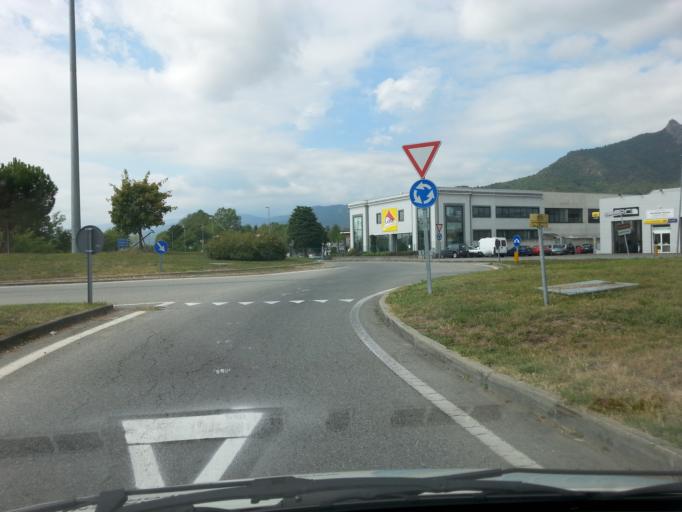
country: IT
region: Piedmont
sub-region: Provincia di Torino
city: Cumiana
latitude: 44.9501
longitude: 7.3934
